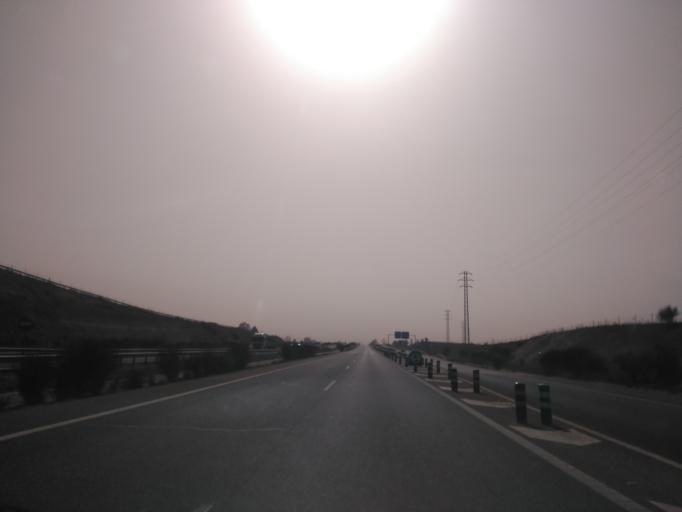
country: ES
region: Castille and Leon
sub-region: Provincia de Palencia
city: Palencia
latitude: 41.9875
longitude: -4.5025
